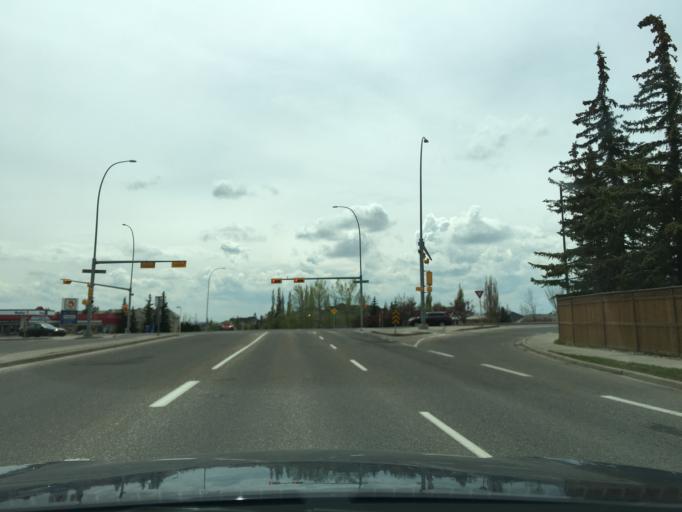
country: CA
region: Alberta
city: Calgary
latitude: 50.9400
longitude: -114.0855
